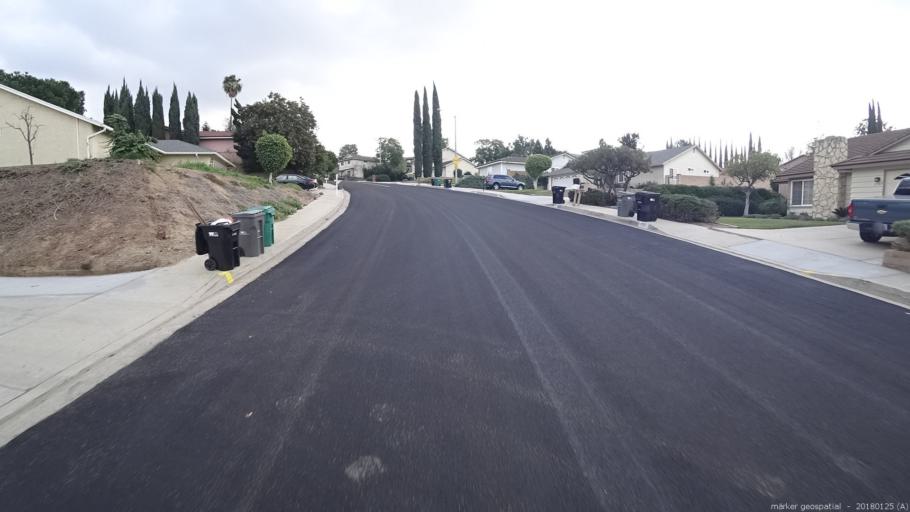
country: US
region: California
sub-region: Los Angeles County
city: Walnut
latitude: 33.9885
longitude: -117.8401
